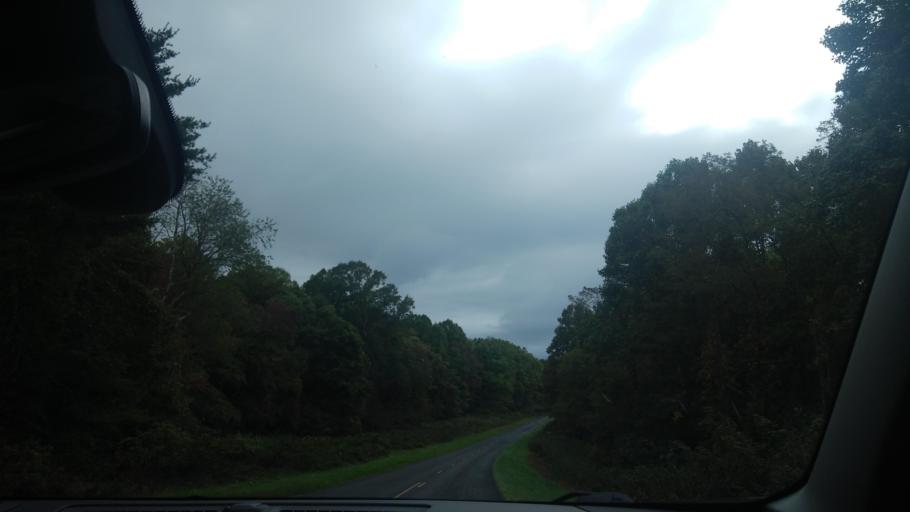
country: US
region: North Carolina
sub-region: Surry County
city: Flat Rock
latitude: 36.6426
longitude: -80.5447
